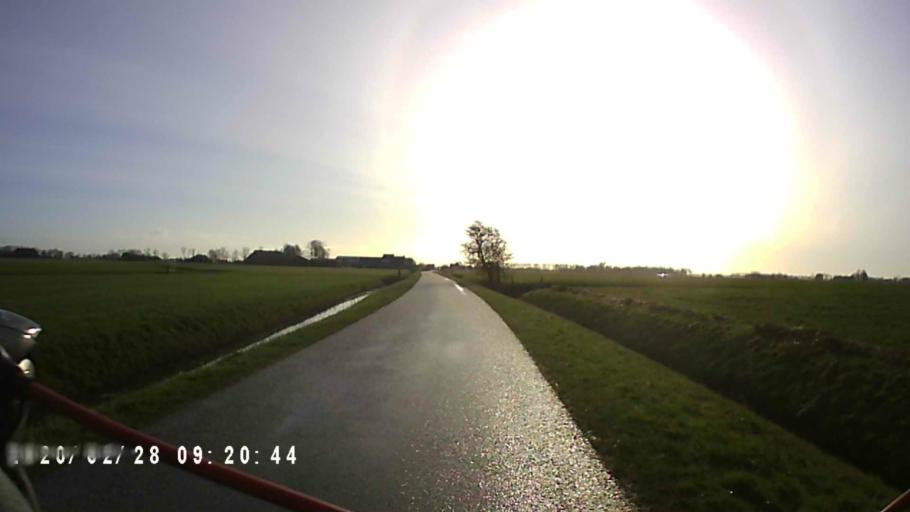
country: NL
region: Groningen
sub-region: Gemeente Zuidhorn
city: Oldehove
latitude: 53.2829
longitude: 6.4057
